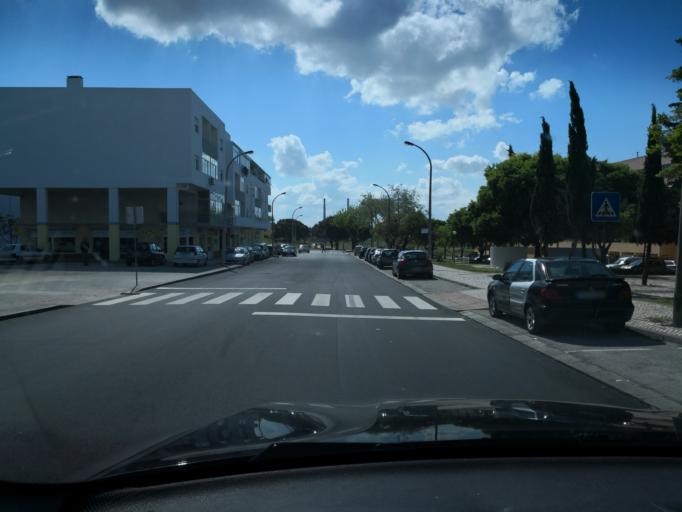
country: PT
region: Setubal
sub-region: Setubal
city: Setubal
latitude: 38.5227
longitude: -8.8666
